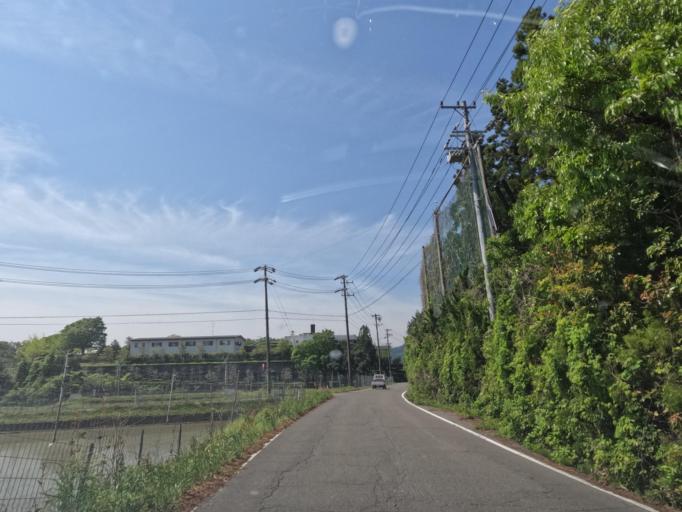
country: JP
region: Mie
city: Komono
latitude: 35.0267
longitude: 136.4826
